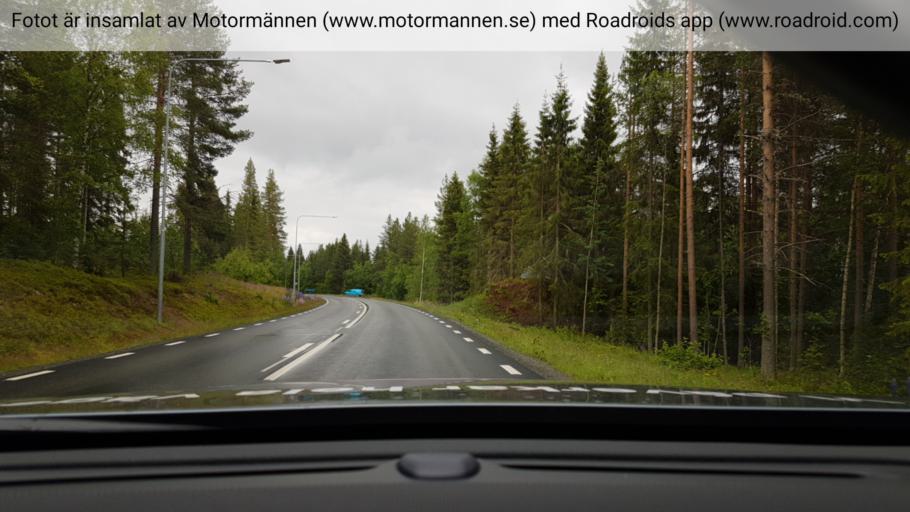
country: SE
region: Vaesterbotten
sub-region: Norsjo Kommun
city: Norsjoe
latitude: 65.2670
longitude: 19.6119
